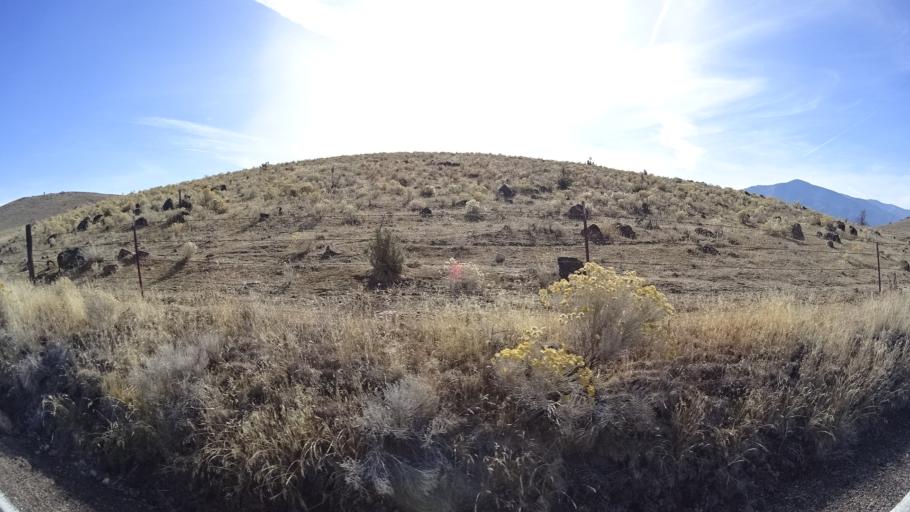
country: US
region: California
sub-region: Siskiyou County
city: Weed
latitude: 41.5490
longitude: -122.4959
